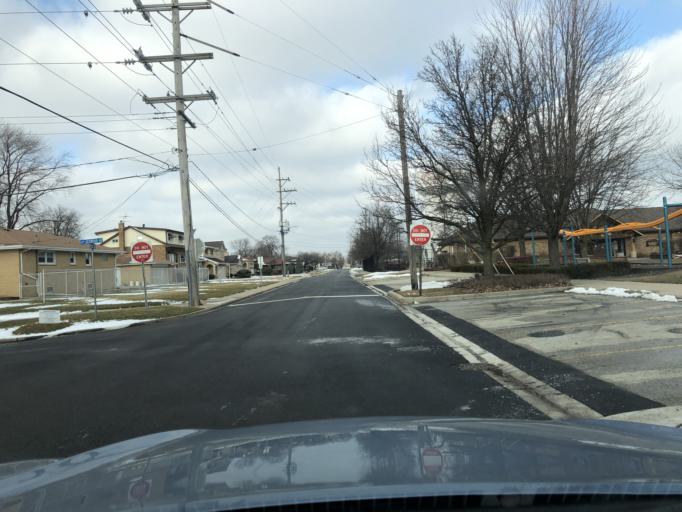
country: US
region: Illinois
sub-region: Cook County
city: Schiller Park
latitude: 41.9510
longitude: -87.8758
